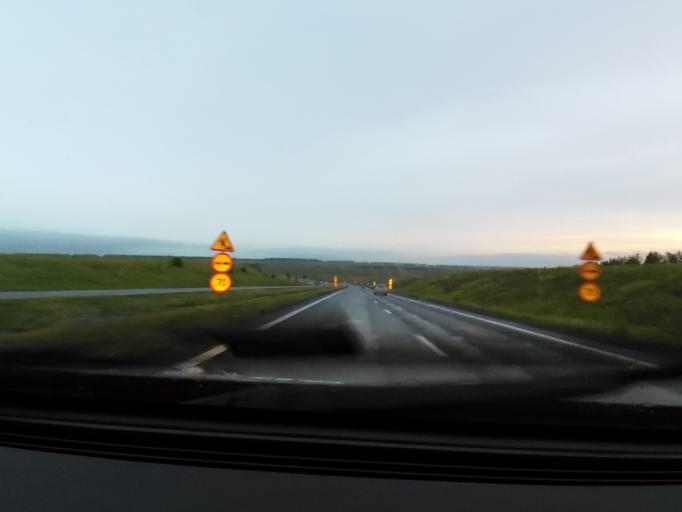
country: RU
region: Tatarstan
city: Yelabuga
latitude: 55.8106
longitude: 51.9668
